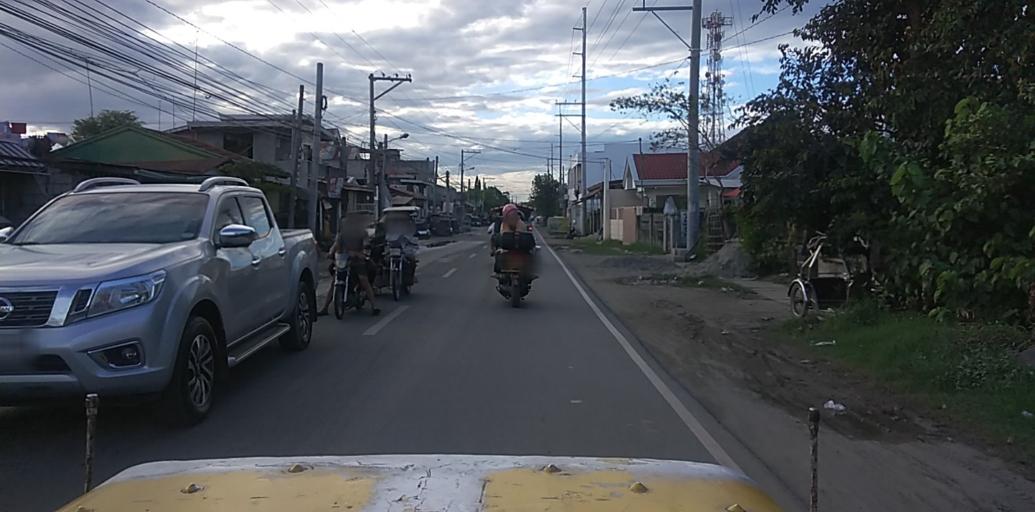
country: PH
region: Central Luzon
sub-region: Province of Pampanga
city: Arayat
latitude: 15.1469
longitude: 120.7647
